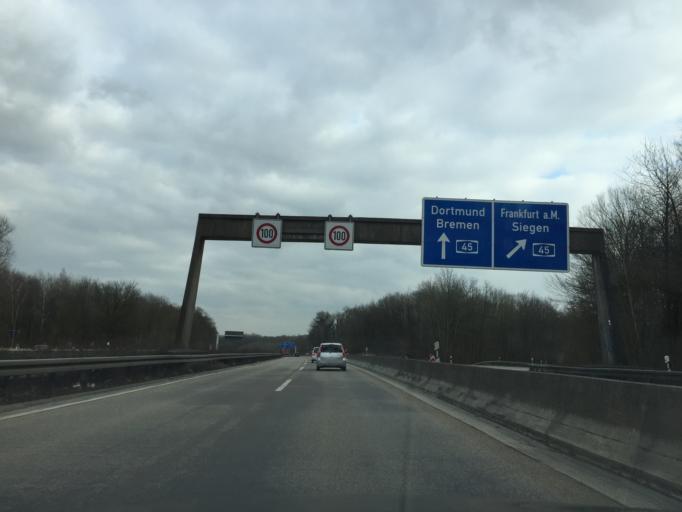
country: DE
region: North Rhine-Westphalia
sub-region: Regierungsbezirk Arnsberg
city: Hagen
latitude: 51.3698
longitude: 7.5126
